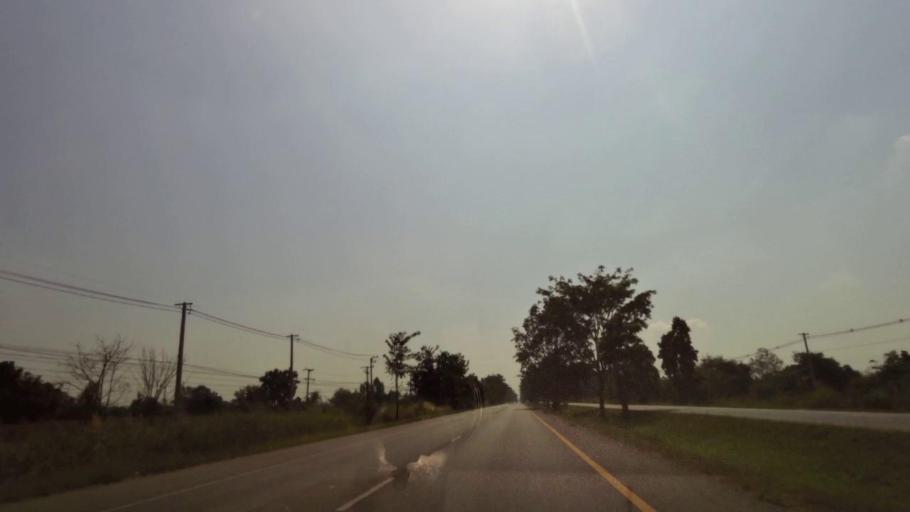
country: TH
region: Phichit
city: Bueng Na Rang
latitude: 16.2880
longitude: 100.1278
